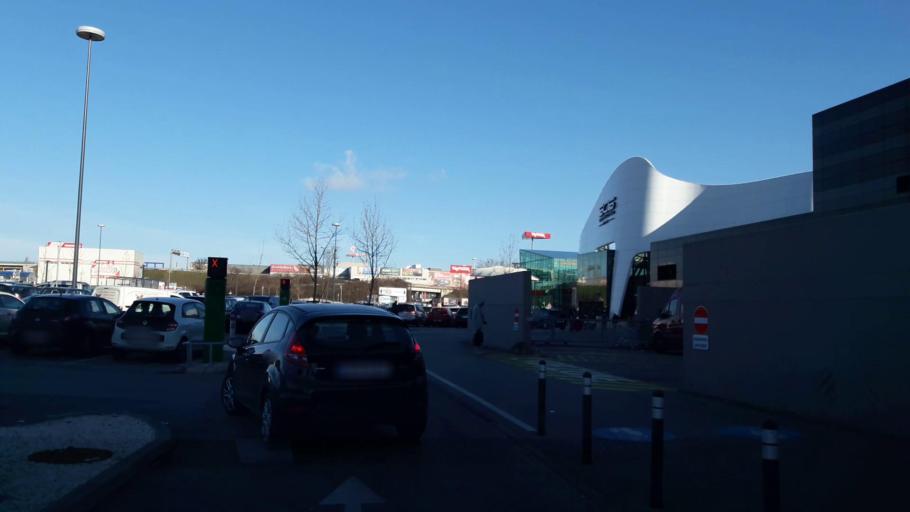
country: AT
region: Lower Austria
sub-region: Politischer Bezirk Modling
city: Vosendorf
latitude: 48.1109
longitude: 16.3172
